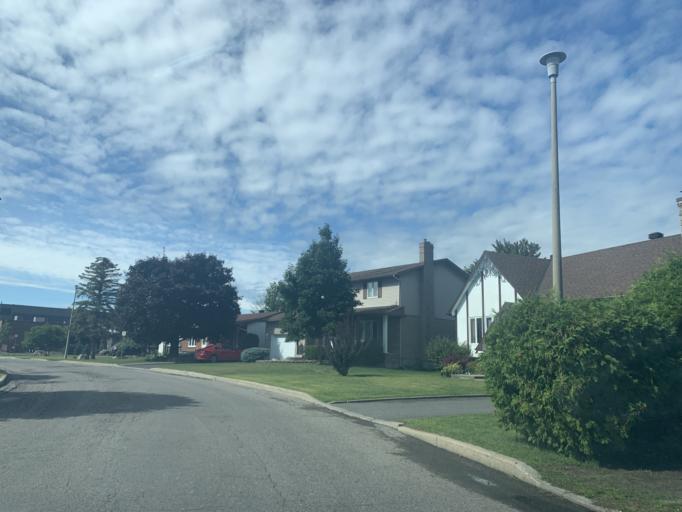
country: CA
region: Ontario
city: Hawkesbury
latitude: 45.6011
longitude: -74.6058
